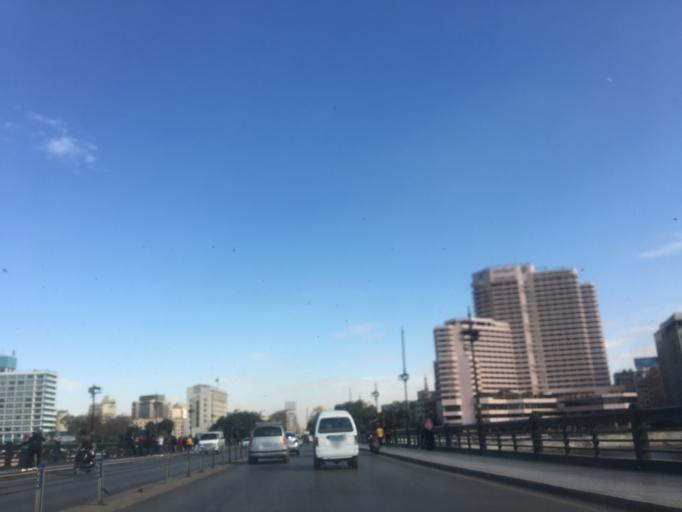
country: EG
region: Muhafazat al Qahirah
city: Cairo
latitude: 30.0436
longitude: 31.2288
